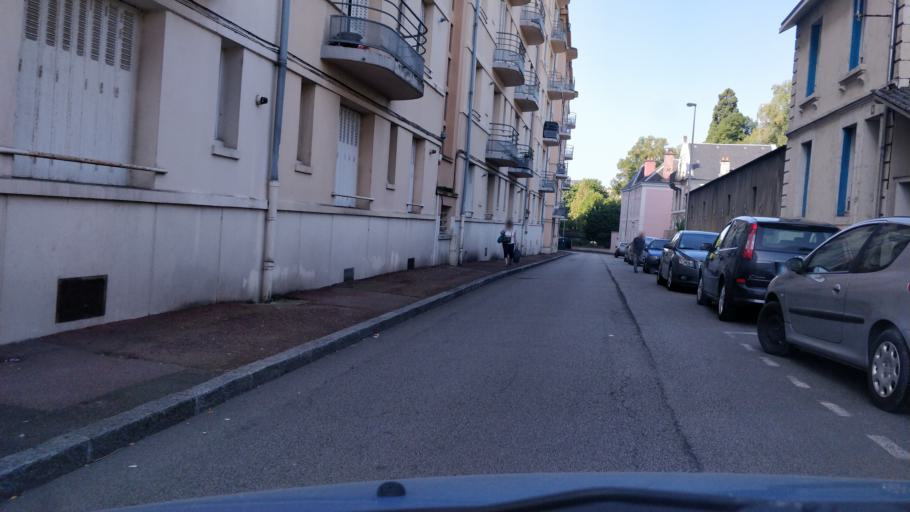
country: FR
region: Limousin
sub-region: Departement de la Haute-Vienne
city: Limoges
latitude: 45.8436
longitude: 1.2566
